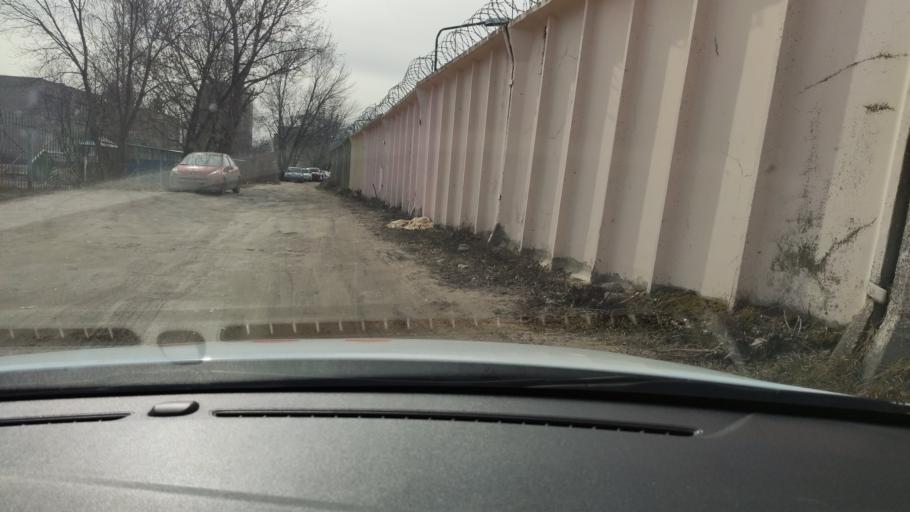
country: RU
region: Tatarstan
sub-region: Gorod Kazan'
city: Kazan
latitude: 55.7498
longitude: 49.1384
